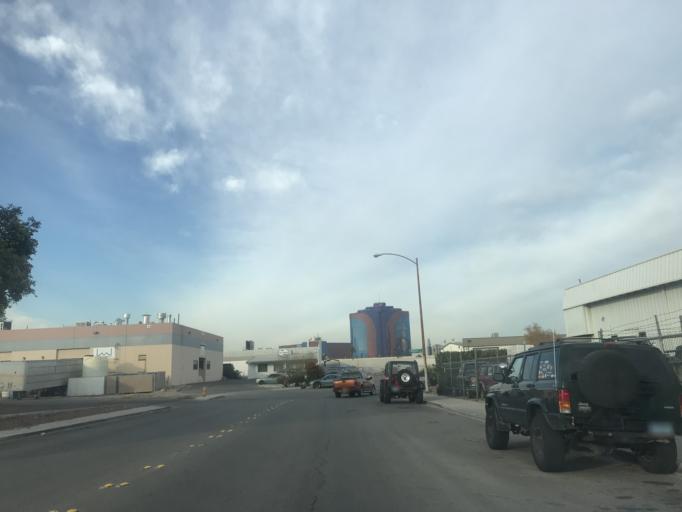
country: US
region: Nevada
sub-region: Clark County
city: Paradise
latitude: 36.1059
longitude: -115.1877
